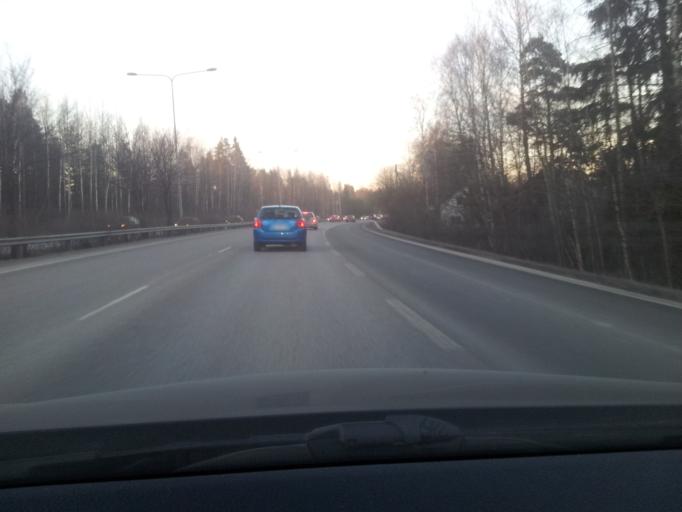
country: FI
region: Uusimaa
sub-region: Helsinki
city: Otaniemi
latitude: 60.1974
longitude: 24.8067
